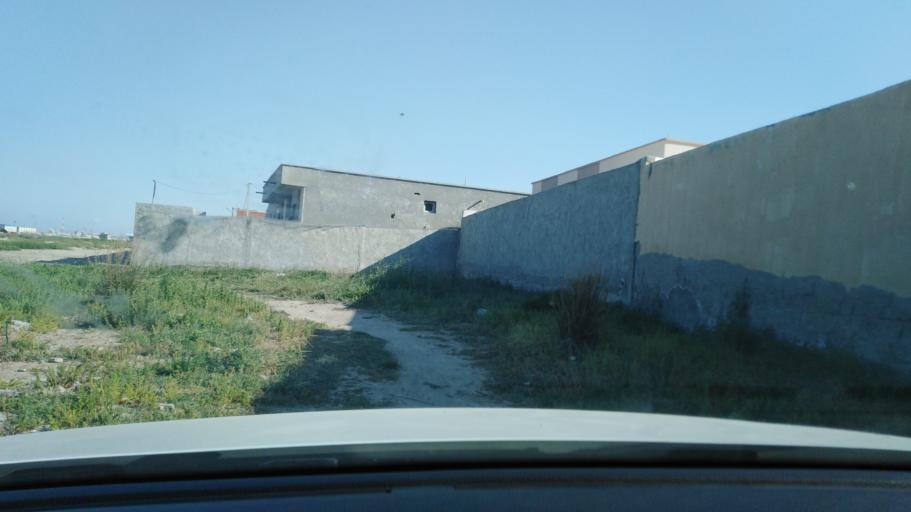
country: TN
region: Qabis
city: Gabes
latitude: 33.9431
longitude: 10.0771
